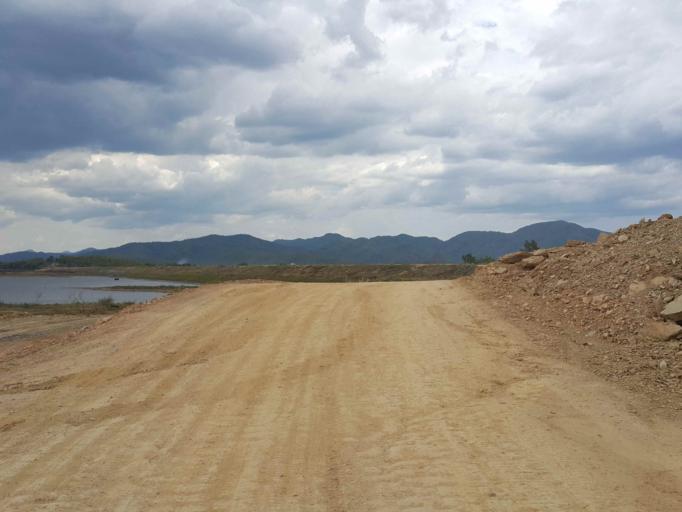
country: TH
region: Sukhothai
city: Thung Saliam
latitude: 17.3097
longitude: 99.4245
